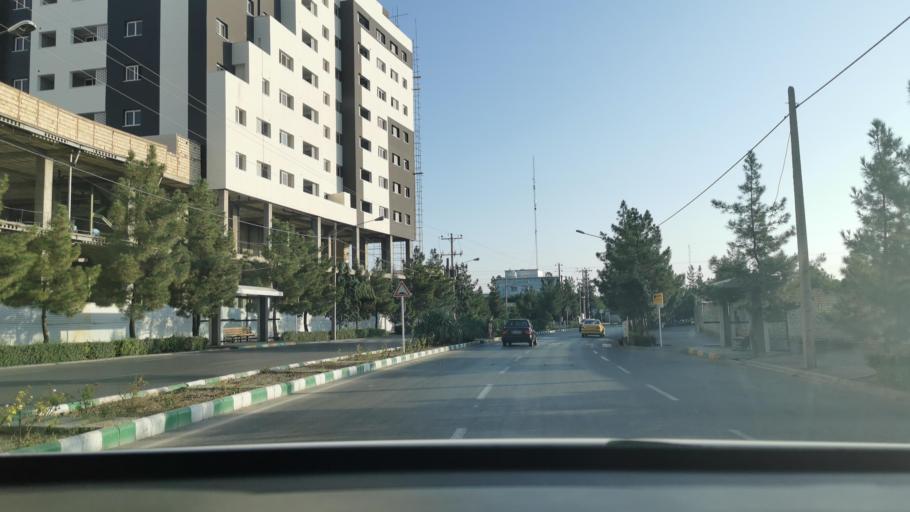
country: IR
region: Razavi Khorasan
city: Mashhad
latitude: 36.3608
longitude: 59.5134
